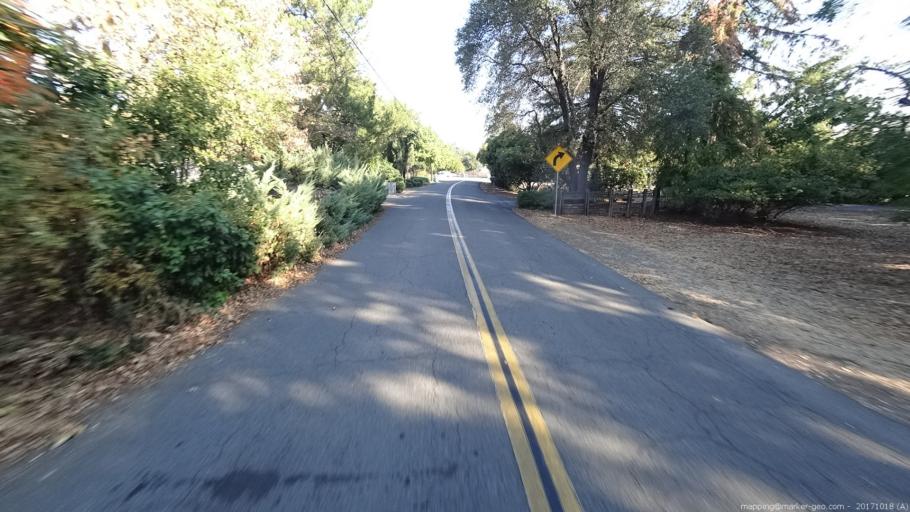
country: US
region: California
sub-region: Shasta County
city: Redding
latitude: 40.5601
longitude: -122.3728
